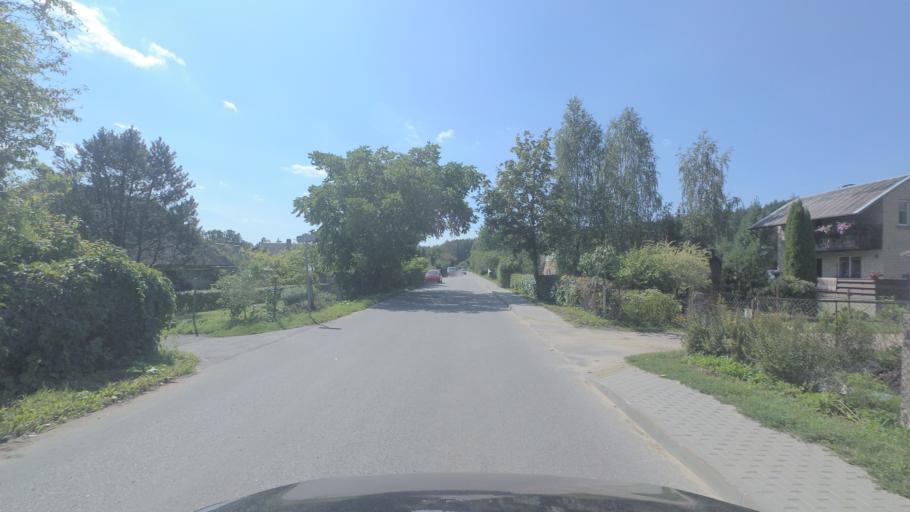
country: LT
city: Nemencine
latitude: 54.8562
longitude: 25.3819
